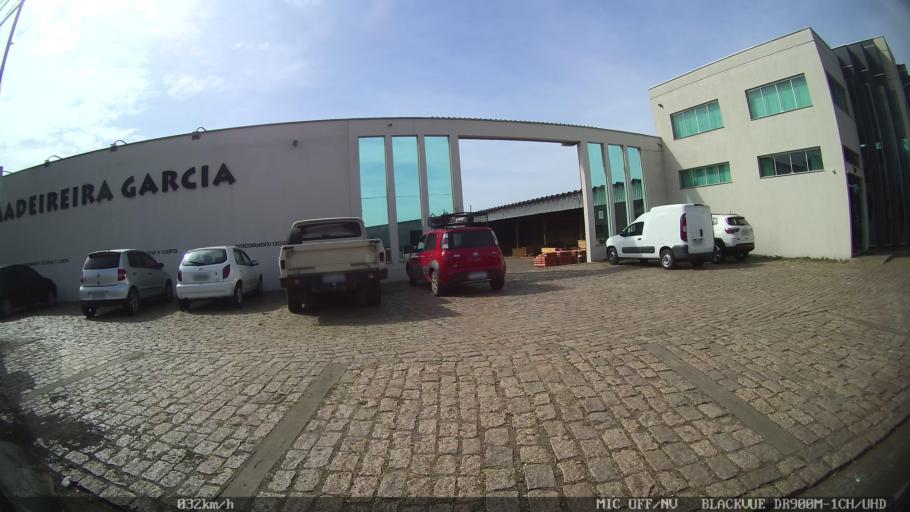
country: BR
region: Sao Paulo
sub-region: Piracicaba
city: Piracicaba
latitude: -22.7526
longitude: -47.6366
